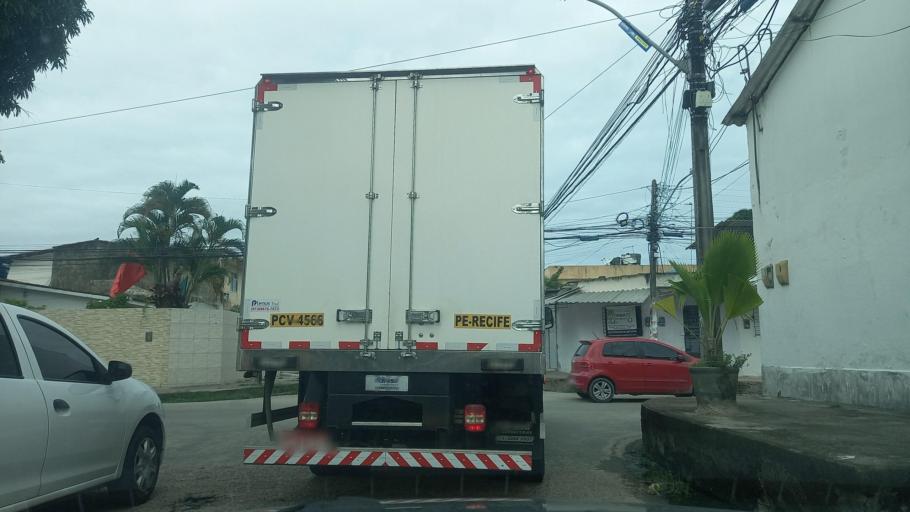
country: BR
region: Pernambuco
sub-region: Recife
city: Recife
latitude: -8.1096
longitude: -34.9214
